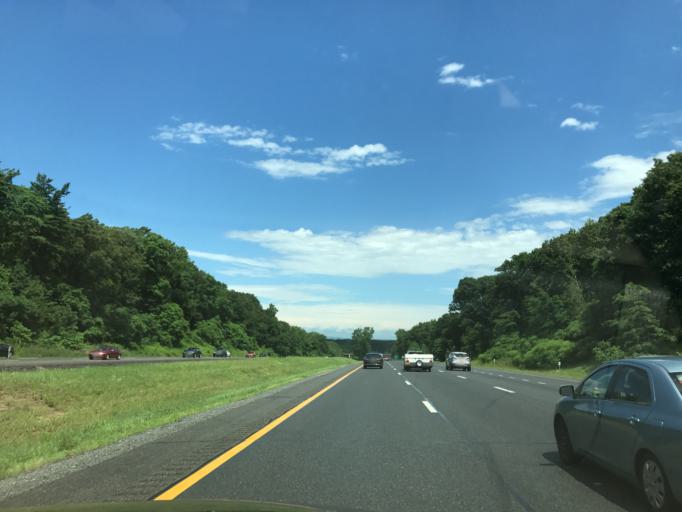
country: US
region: New York
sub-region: Saratoga County
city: Country Knolls
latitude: 42.8801
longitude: -73.7779
